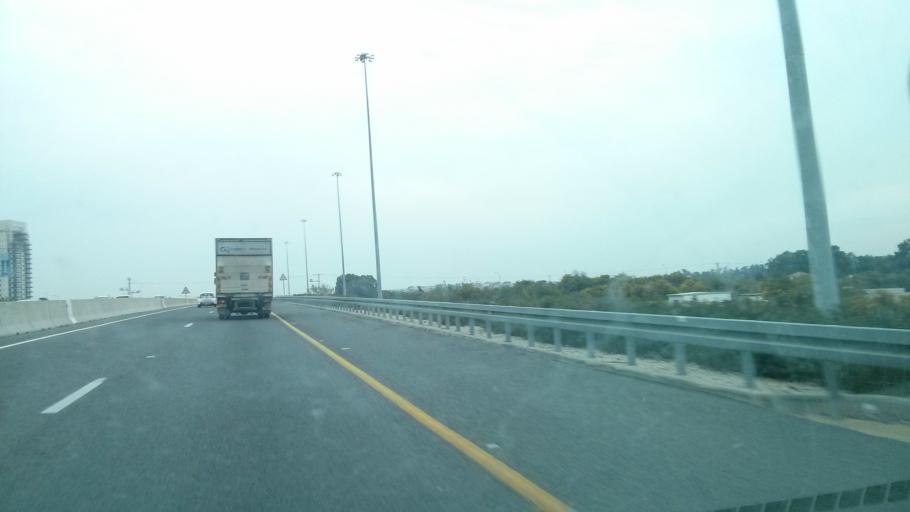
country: IL
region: Haifa
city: Qesarya
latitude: 32.5074
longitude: 34.9130
